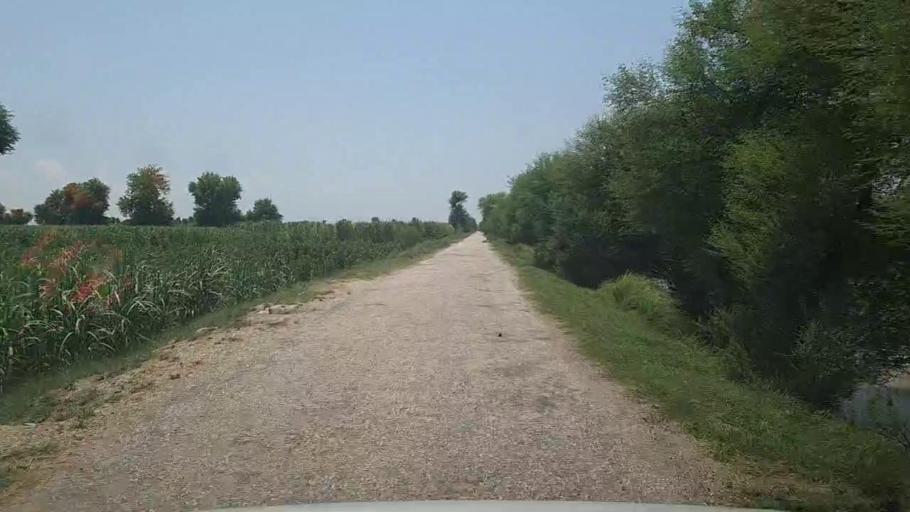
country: PK
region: Sindh
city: Ubauro
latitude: 28.1633
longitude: 69.7462
